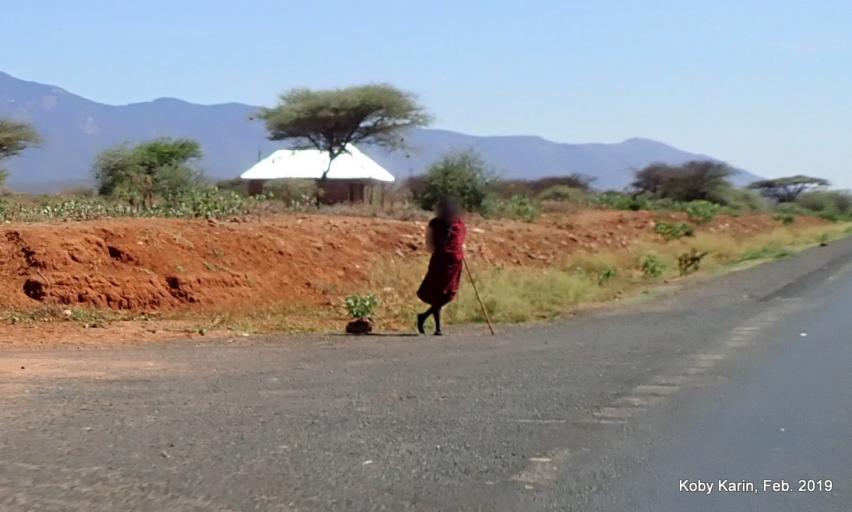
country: TZ
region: Arusha
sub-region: Longido District
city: Longido
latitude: -2.6393
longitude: 36.7128
